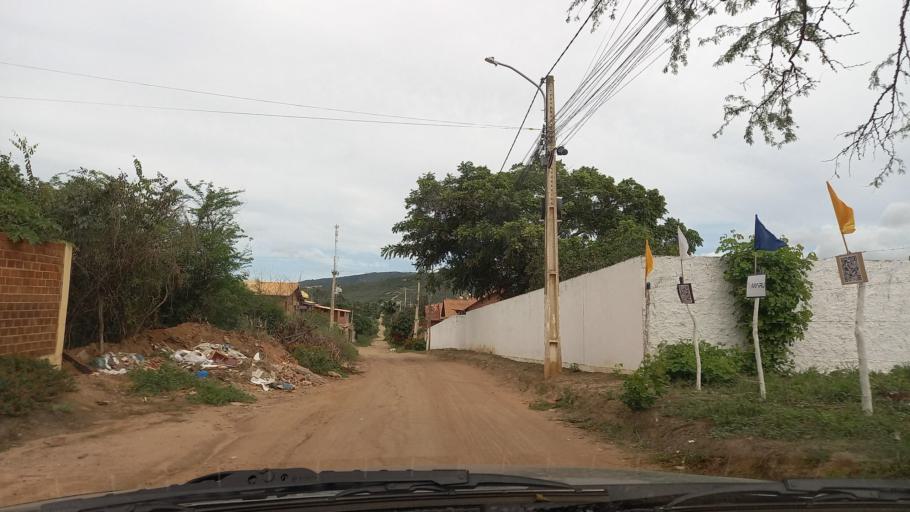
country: BR
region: Pernambuco
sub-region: Gravata
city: Gravata
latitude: -8.1966
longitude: -35.5934
